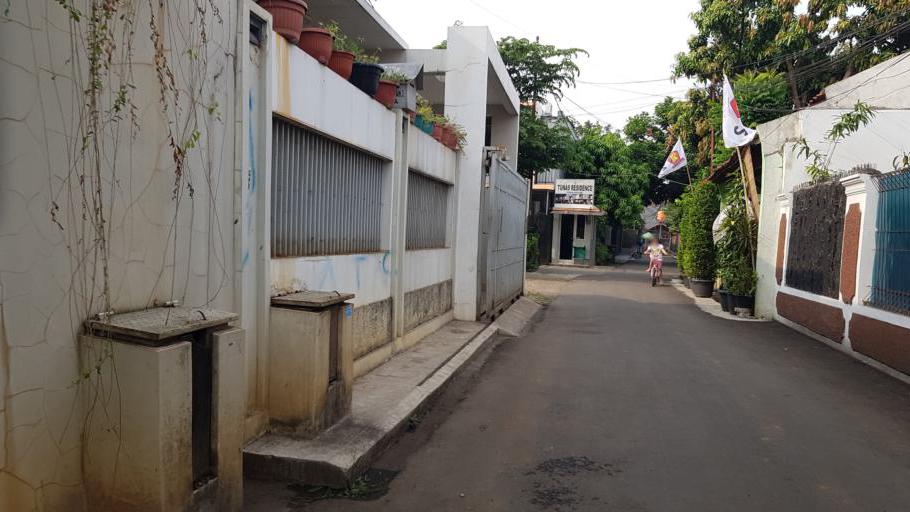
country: ID
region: West Java
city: Pamulang
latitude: -6.3279
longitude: 106.7980
